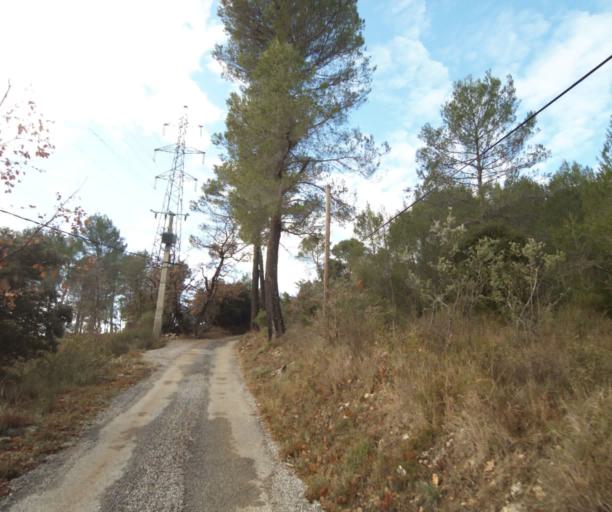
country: FR
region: Provence-Alpes-Cote d'Azur
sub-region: Departement du Var
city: Trans-en-Provence
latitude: 43.4991
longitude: 6.4669
